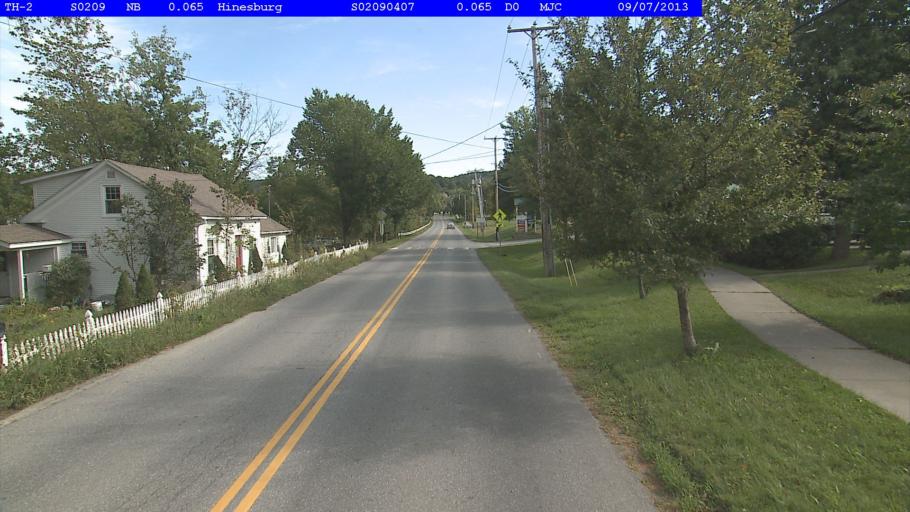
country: US
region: Vermont
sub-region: Chittenden County
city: Hinesburg
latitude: 44.3324
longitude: -73.1098
